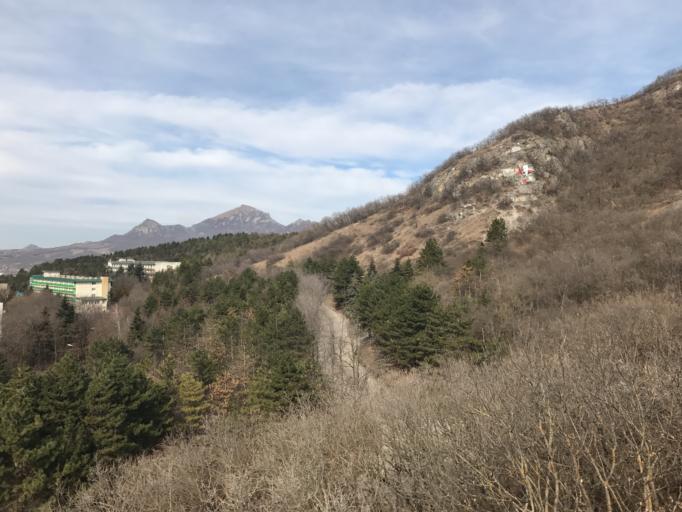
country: RU
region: Stavropol'skiy
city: Goryachevodskiy
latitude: 44.0448
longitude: 43.0826
